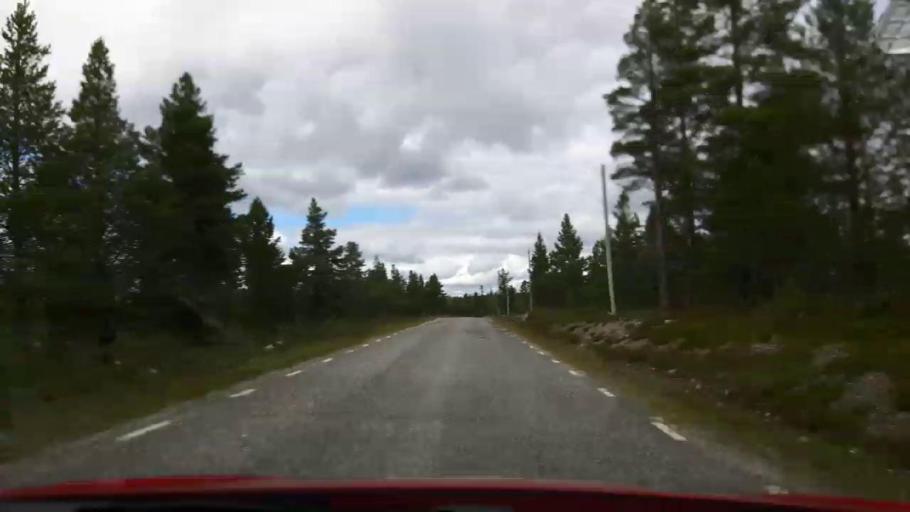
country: NO
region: Hedmark
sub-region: Engerdal
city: Engerdal
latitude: 62.3219
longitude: 12.8089
